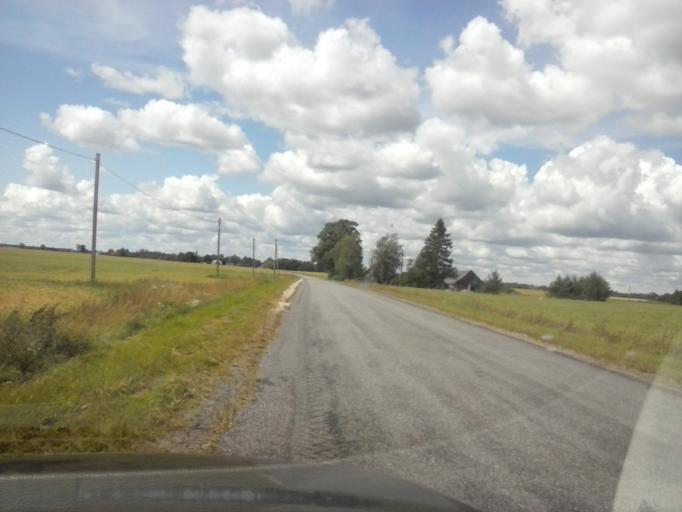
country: EE
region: Laeaene-Virumaa
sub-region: Vaeike-Maarja vald
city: Vaike-Maarja
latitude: 59.0582
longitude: 26.3373
